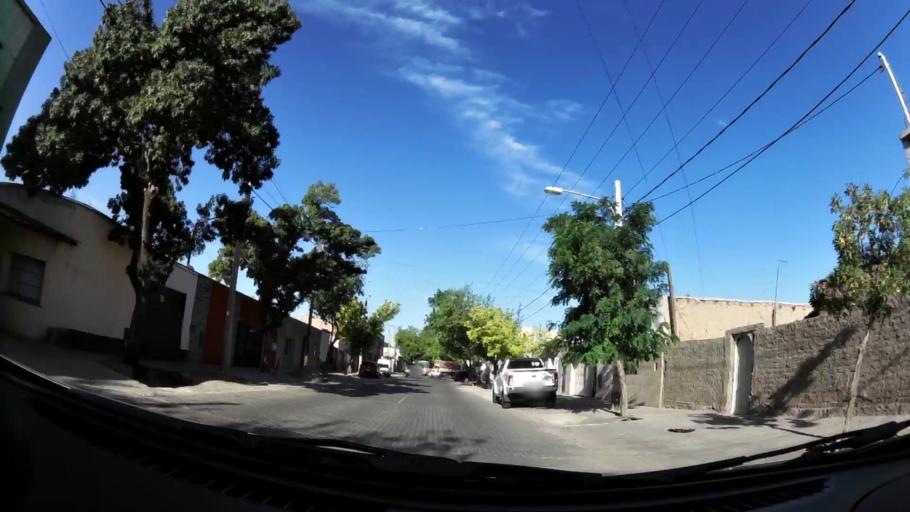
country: AR
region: Mendoza
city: Mendoza
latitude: -32.9032
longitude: -68.8312
